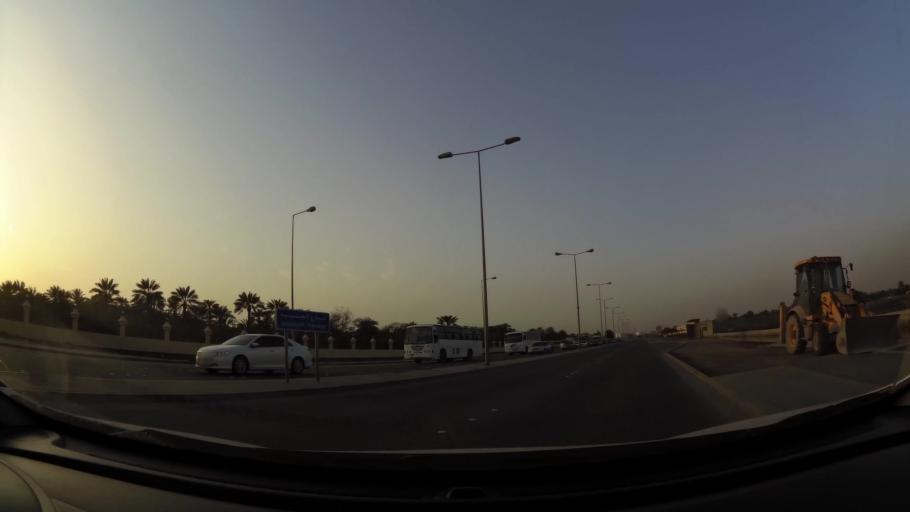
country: BH
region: Central Governorate
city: Madinat Hamad
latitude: 26.1825
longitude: 50.4658
